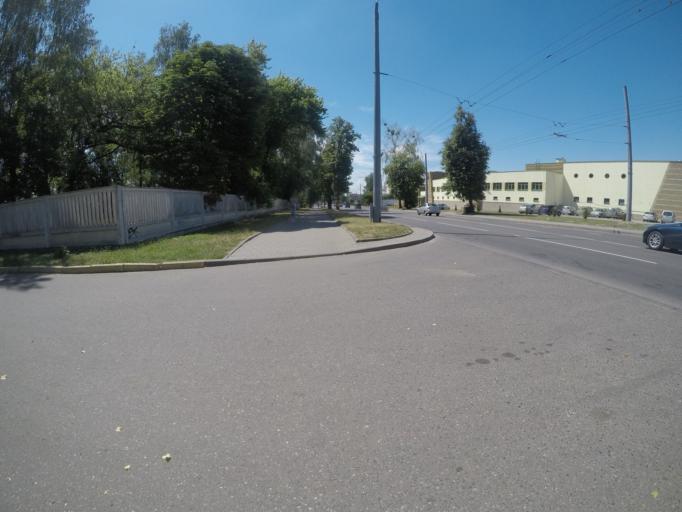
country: BY
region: Grodnenskaya
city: Hrodna
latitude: 53.6936
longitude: 23.8389
